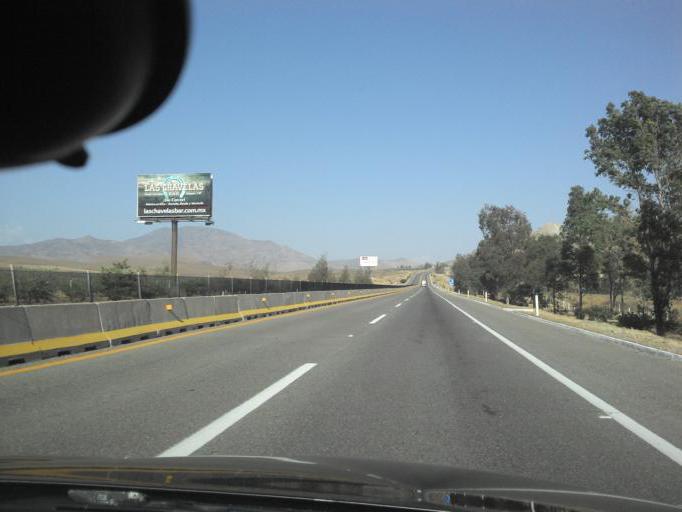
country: MX
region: Baja California
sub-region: Tijuana
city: El Nino
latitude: 32.5457
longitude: -116.7858
